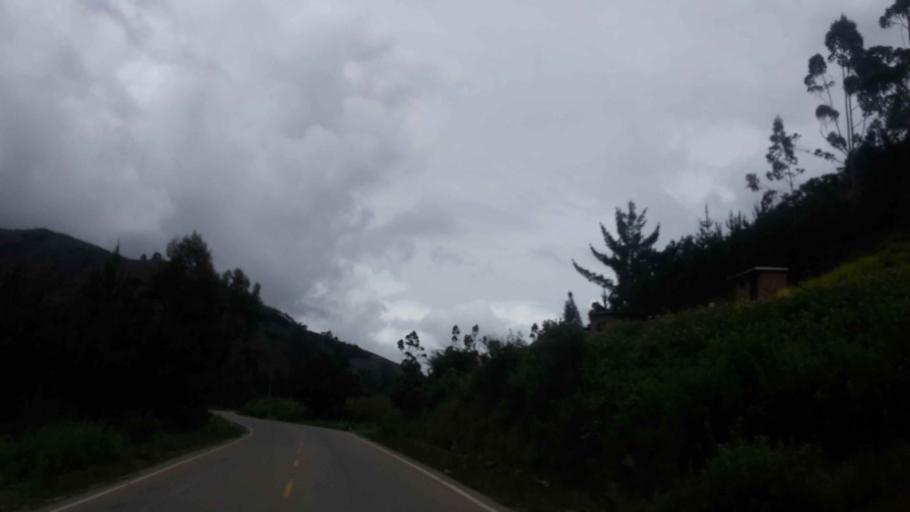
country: BO
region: Cochabamba
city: Arani
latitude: -17.4857
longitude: -65.4708
